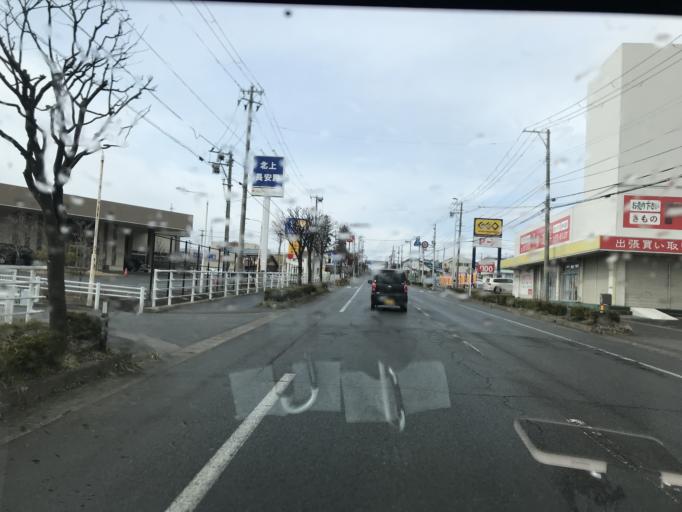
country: JP
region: Iwate
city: Kitakami
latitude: 39.2970
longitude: 141.1185
